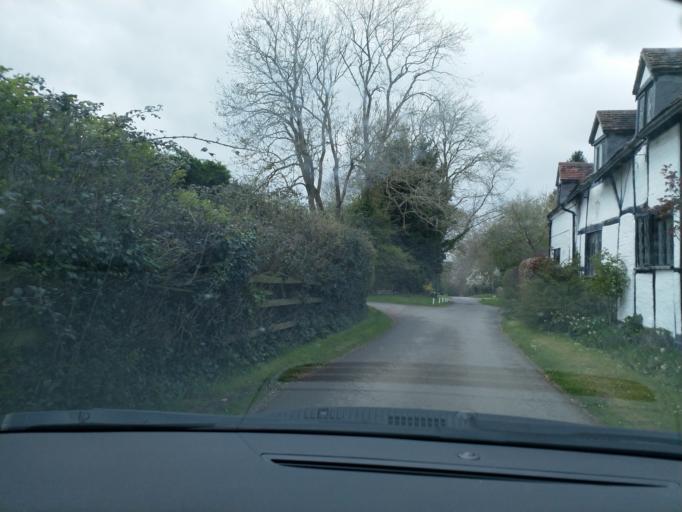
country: GB
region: England
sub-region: Warwickshire
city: Henley in Arden
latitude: 52.2935
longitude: -1.7286
